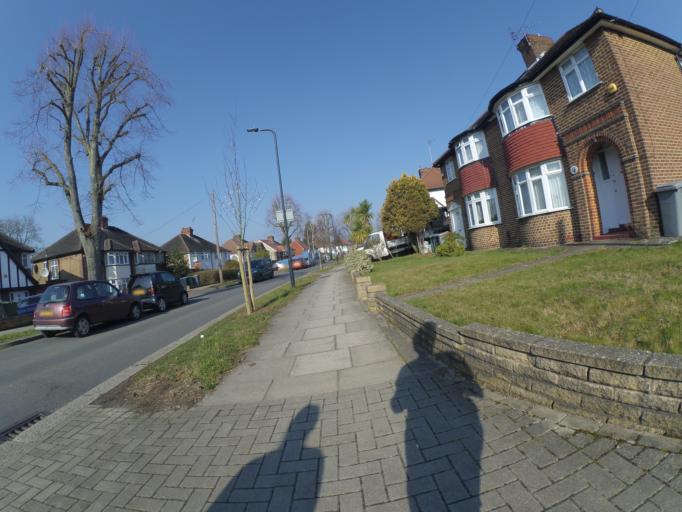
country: GB
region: England
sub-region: Greater London
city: Wembley
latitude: 51.5727
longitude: -0.2891
